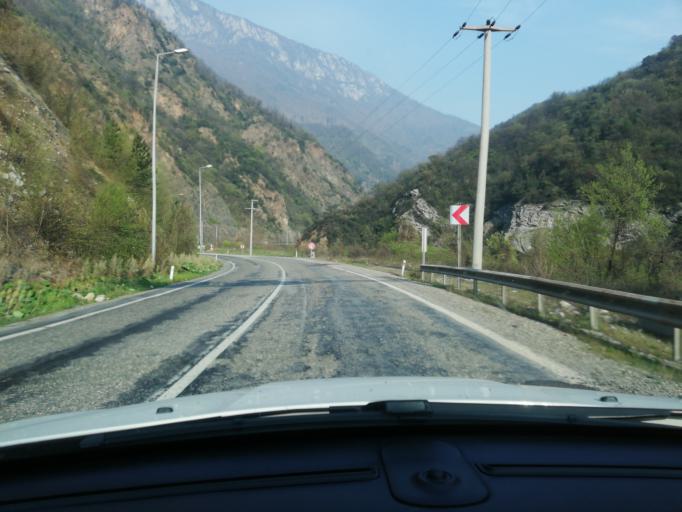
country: TR
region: Karabuk
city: Yenice
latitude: 41.1582
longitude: 32.4640
